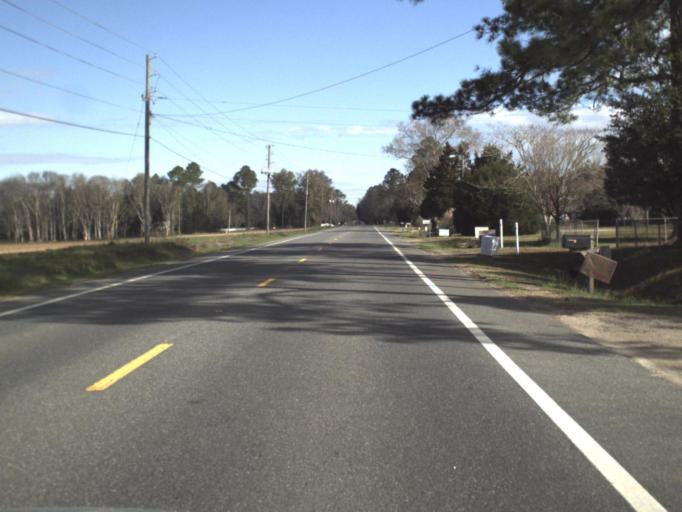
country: US
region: Florida
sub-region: Jackson County
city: Malone
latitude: 30.8556
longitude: -85.1639
